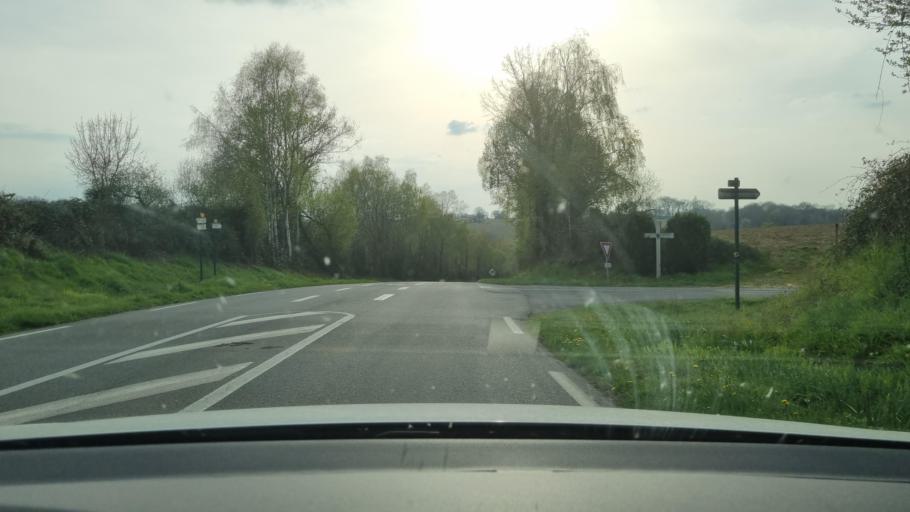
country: FR
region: Aquitaine
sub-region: Departement des Pyrenees-Atlantiques
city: Morlaas
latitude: 43.3716
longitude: -0.1761
